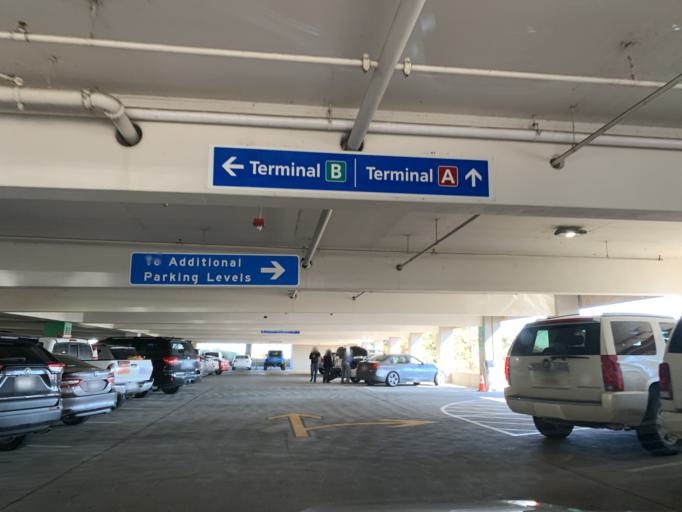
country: US
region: California
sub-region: Yolo County
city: West Sacramento
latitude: 38.6898
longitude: -121.5831
